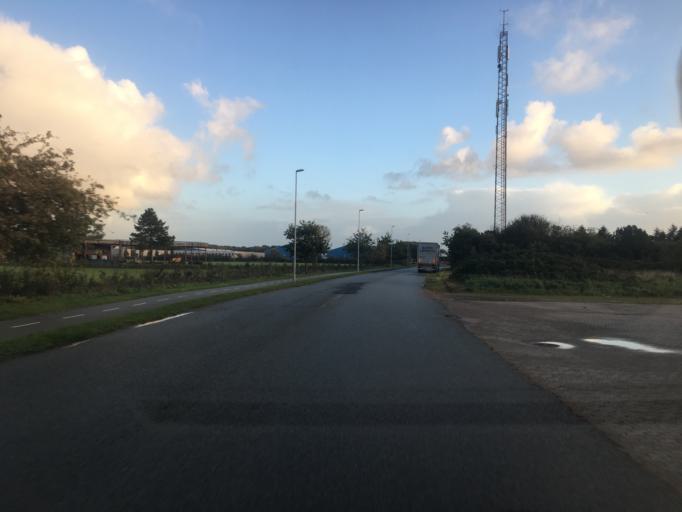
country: DK
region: South Denmark
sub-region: Tonder Kommune
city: Tonder
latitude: 54.9296
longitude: 8.8514
